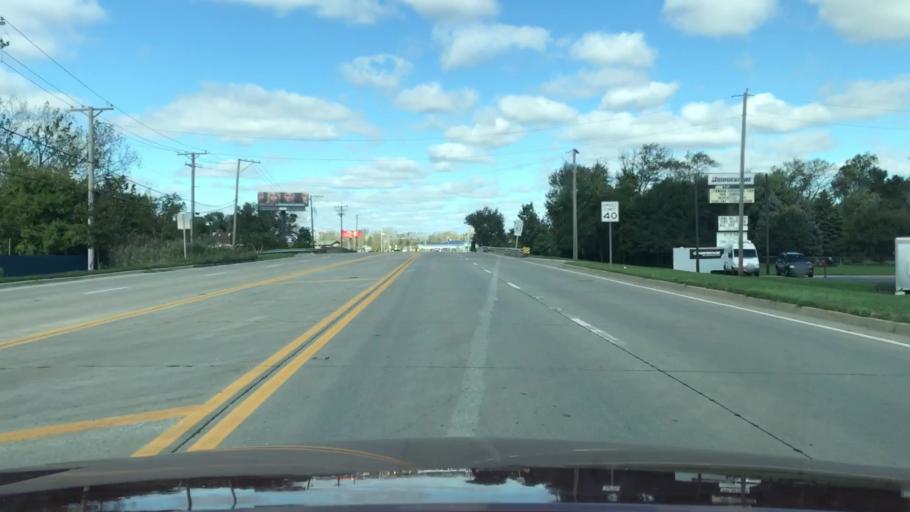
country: US
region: Indiana
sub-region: Lake County
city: Dyer
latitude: 41.5031
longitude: -87.5309
